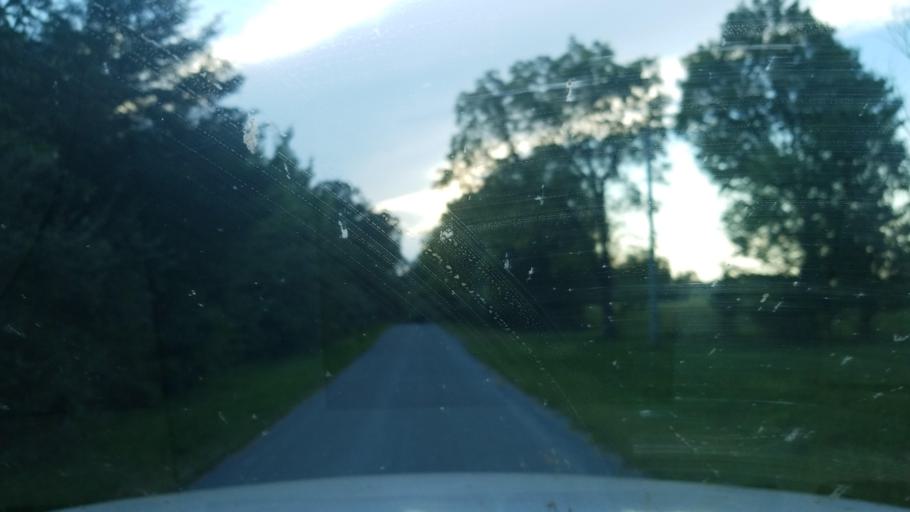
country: US
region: Illinois
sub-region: Saline County
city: Carrier Mills
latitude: 37.7903
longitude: -88.7027
